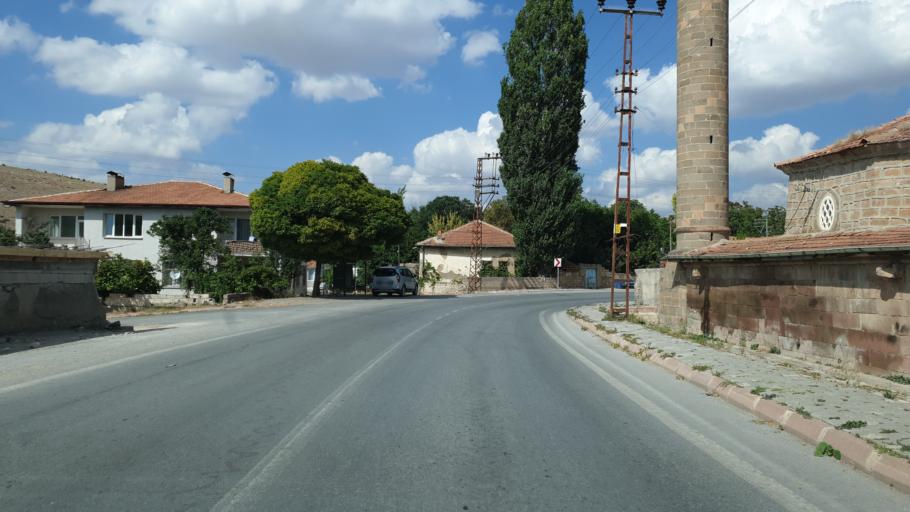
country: TR
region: Kayseri
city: Felahiye
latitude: 39.0931
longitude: 35.5696
